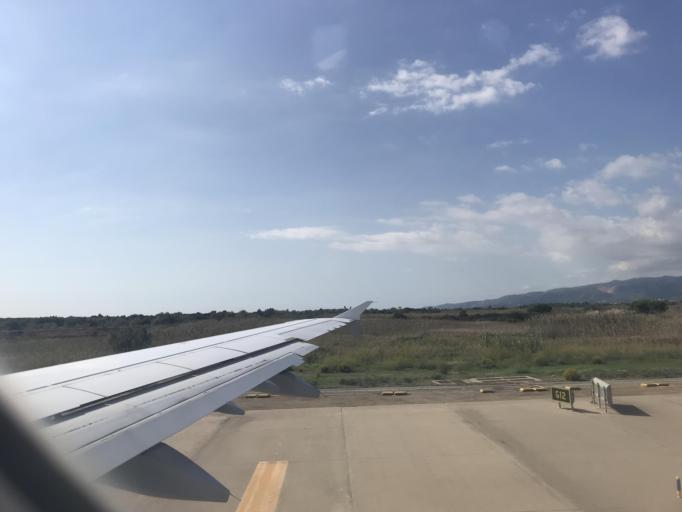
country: ES
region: Catalonia
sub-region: Provincia de Barcelona
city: El Prat de Llobregat
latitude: 41.2827
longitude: 2.0736
